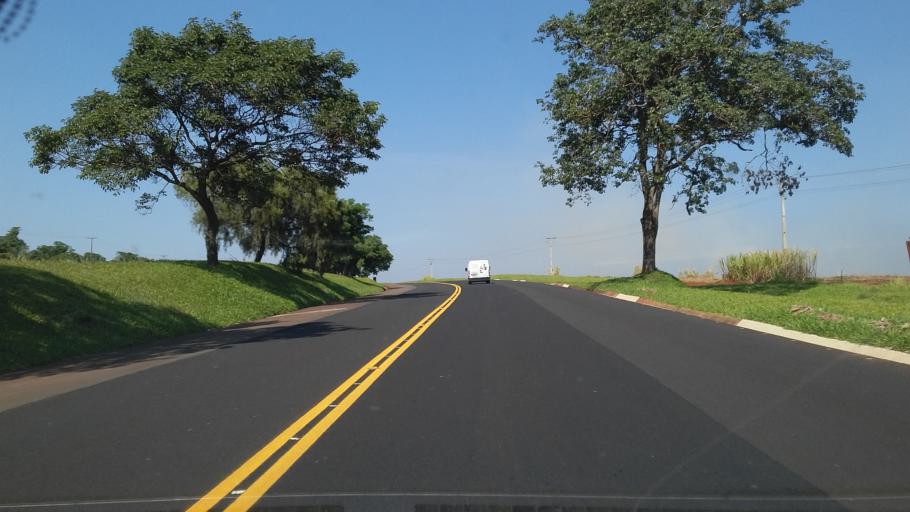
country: BR
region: Parana
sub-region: Bandeirantes
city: Bandeirantes
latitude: -23.1293
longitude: -50.4673
